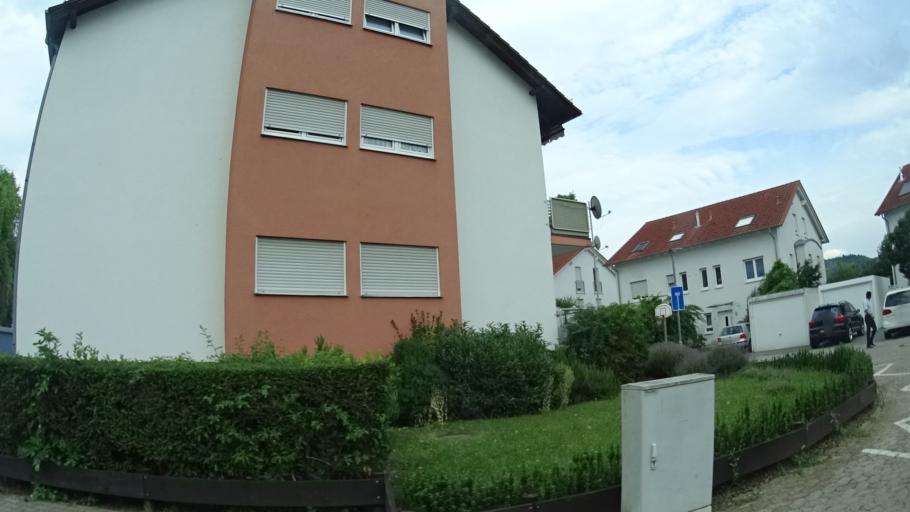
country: DE
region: Hesse
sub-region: Regierungsbezirk Darmstadt
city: Bensheim
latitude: 49.7015
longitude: 8.6153
